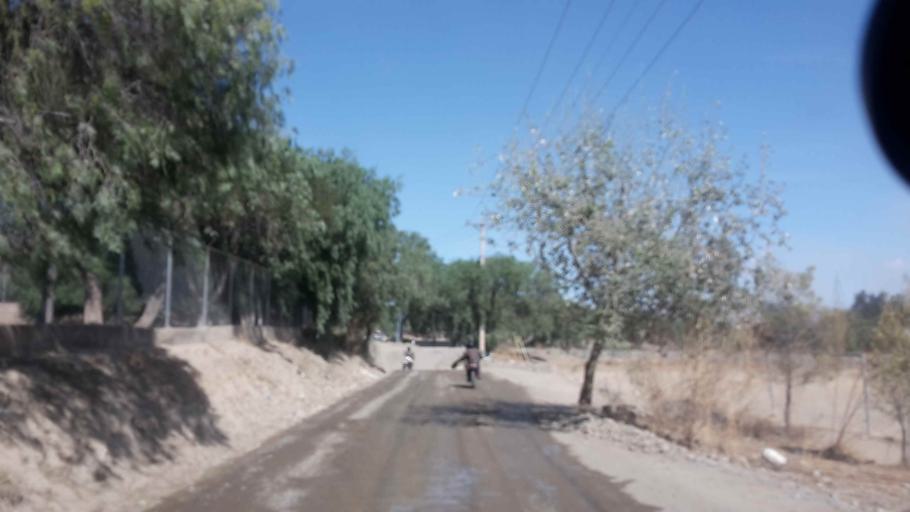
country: BO
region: Cochabamba
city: Cochabamba
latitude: -17.3382
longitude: -66.2140
